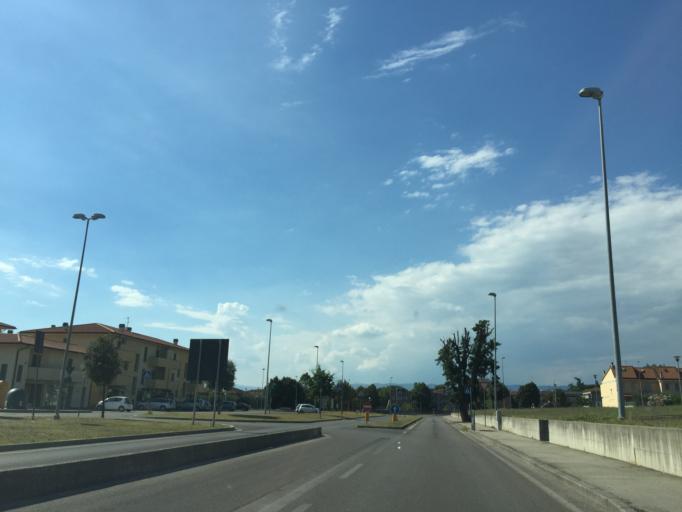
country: IT
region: Tuscany
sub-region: Provincia di Pistoia
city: Lamporecchio
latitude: 43.8198
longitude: 10.8745
